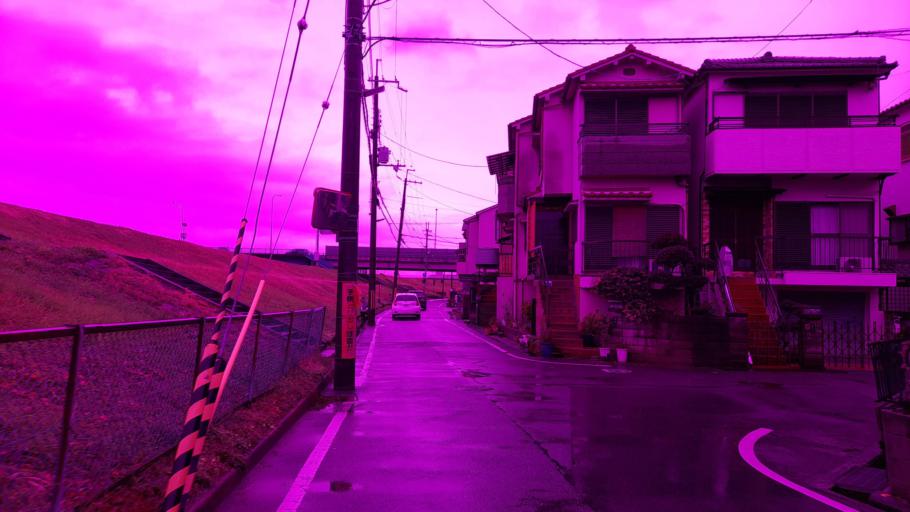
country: JP
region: Osaka
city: Toyonaka
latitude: 34.7591
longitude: 135.4558
